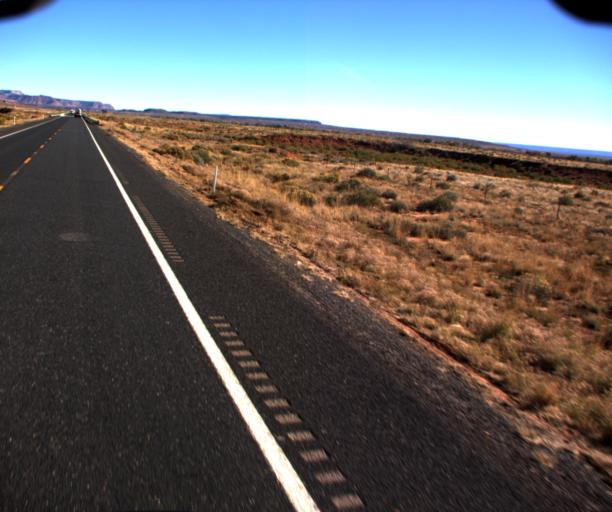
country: US
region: Arizona
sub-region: Coconino County
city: Fredonia
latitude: 36.9263
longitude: -112.5664
